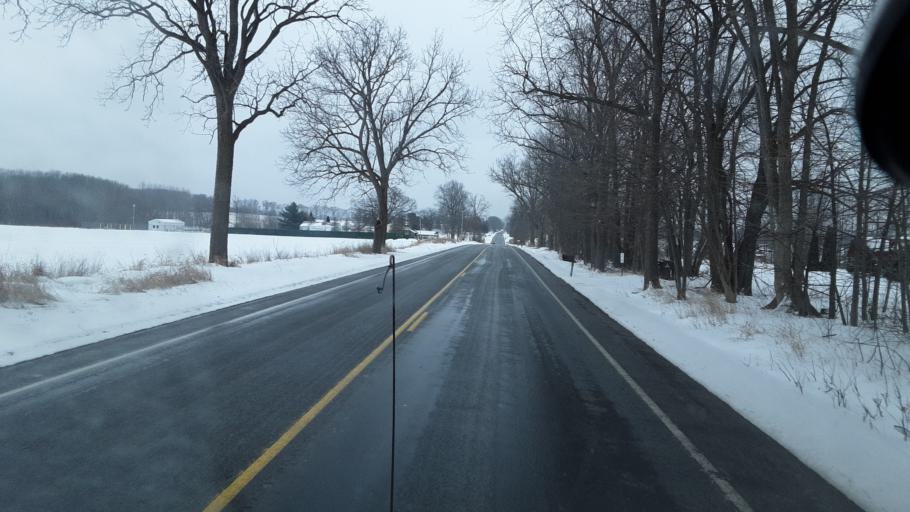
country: US
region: Michigan
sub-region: Ingham County
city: Leslie
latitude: 42.4318
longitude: -84.4137
